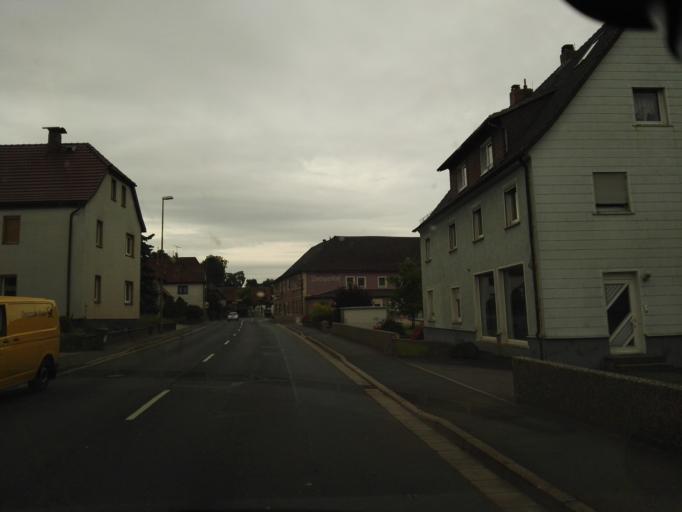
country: DE
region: Bavaria
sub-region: Upper Franconia
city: Burgkunstadt
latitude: 50.1458
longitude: 11.2283
